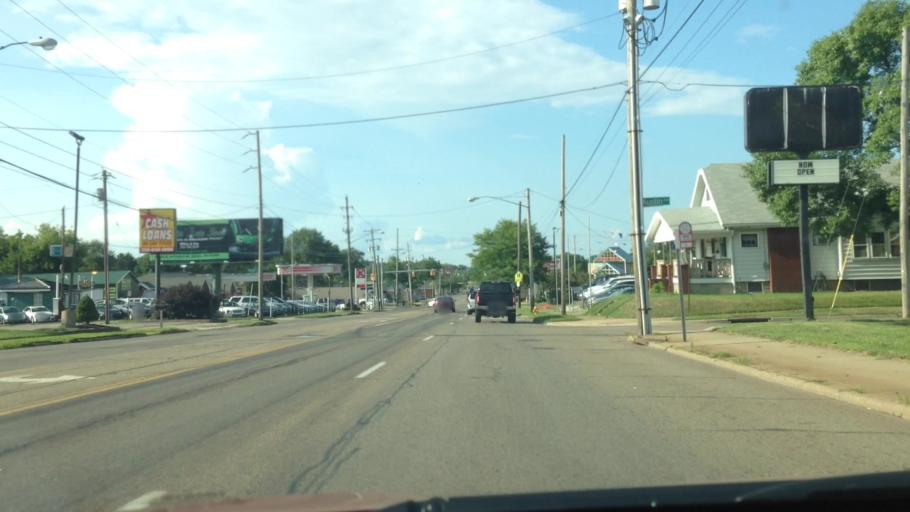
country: US
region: Ohio
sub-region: Summit County
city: Akron
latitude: 41.0453
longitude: -81.4911
